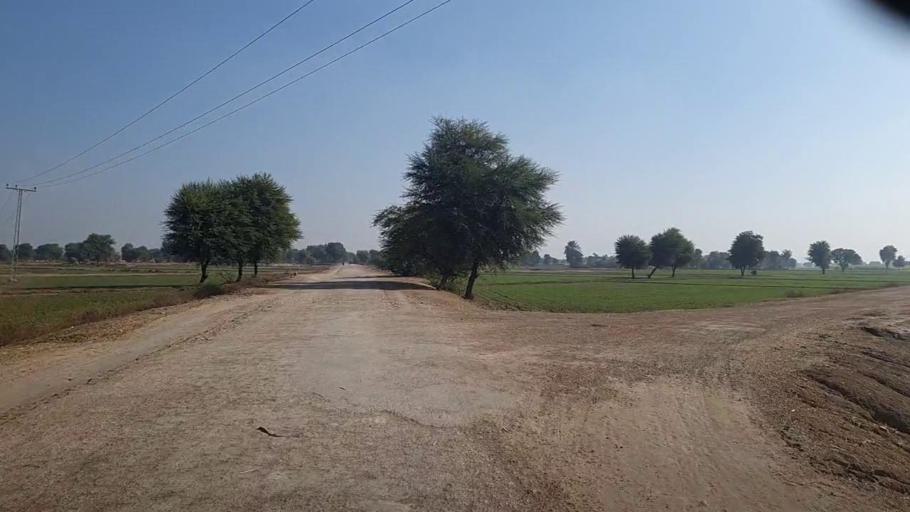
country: PK
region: Sindh
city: Darya Khan Marri
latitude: 26.6660
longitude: 68.3362
